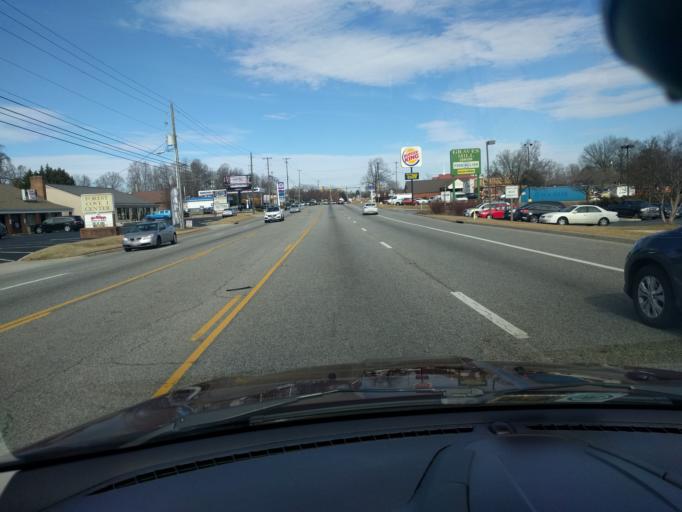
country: US
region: Virginia
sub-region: Bedford County
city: Forest
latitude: 37.3768
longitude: -79.2488
